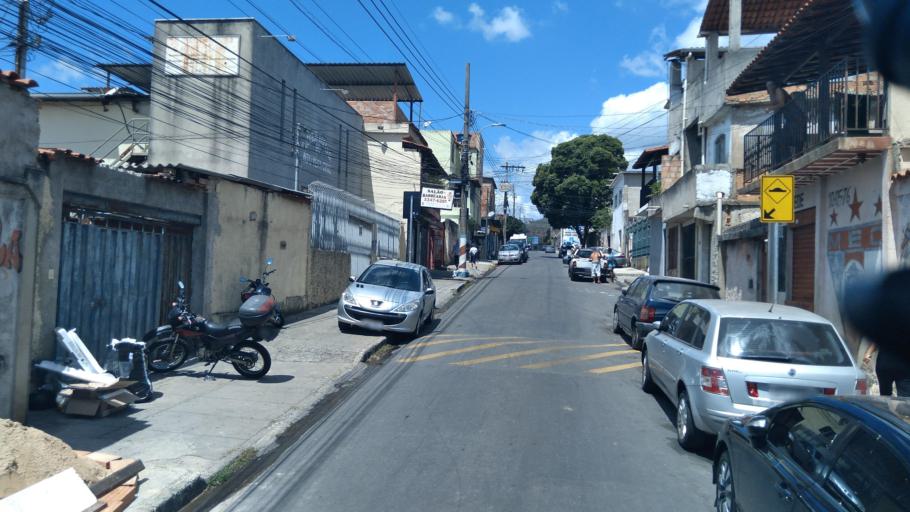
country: BR
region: Minas Gerais
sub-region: Belo Horizonte
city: Belo Horizonte
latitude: -19.9083
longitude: -43.8897
